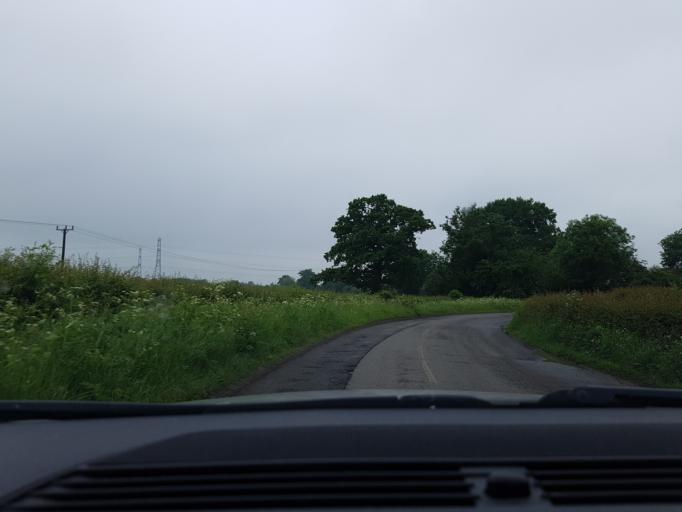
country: GB
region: England
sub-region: Buckinghamshire
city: Winslow
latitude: 51.9391
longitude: -0.9238
